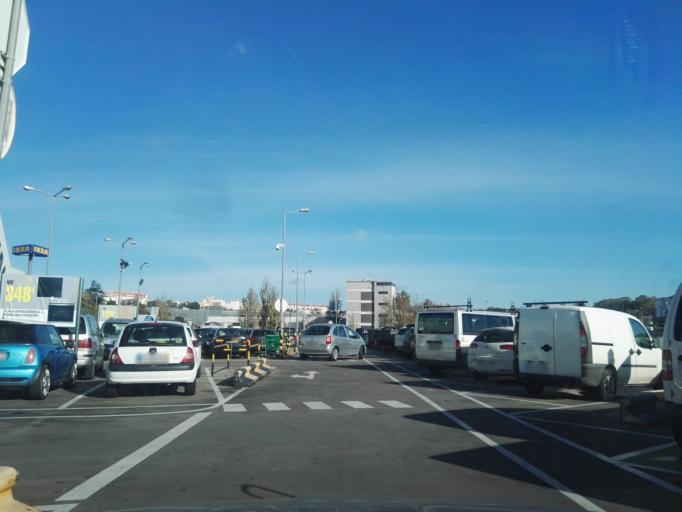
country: PT
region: Lisbon
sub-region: Oeiras
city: Alges
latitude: 38.7252
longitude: -9.2157
